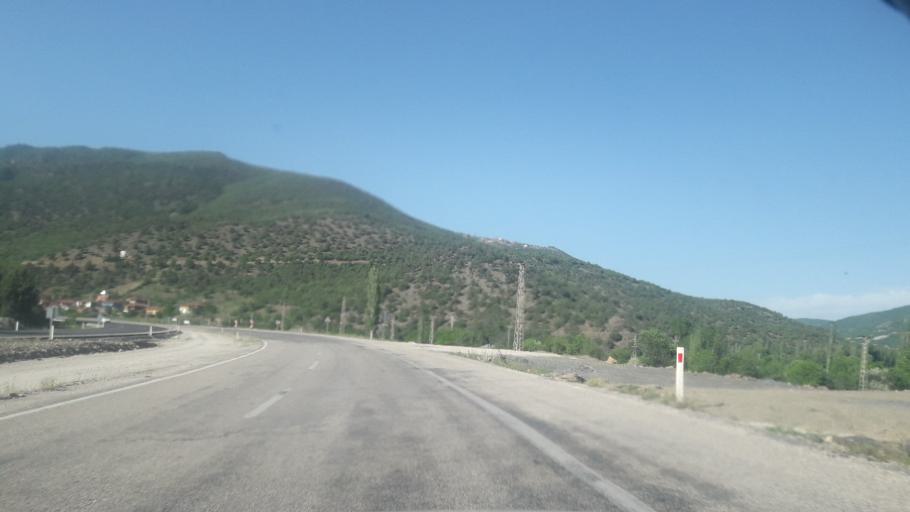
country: TR
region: Tokat
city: Turhal
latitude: 40.4787
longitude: 36.1551
